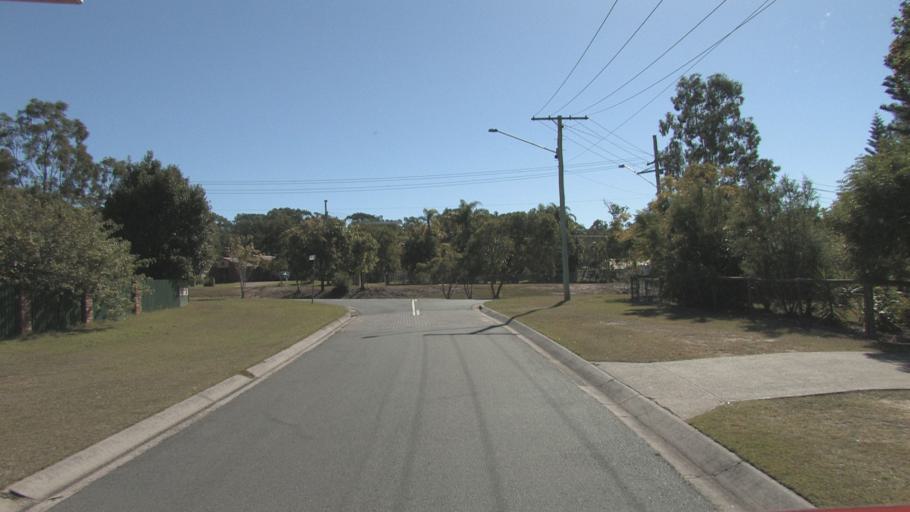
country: AU
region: Queensland
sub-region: Logan
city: Logan Reserve
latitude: -27.6796
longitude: 153.0665
